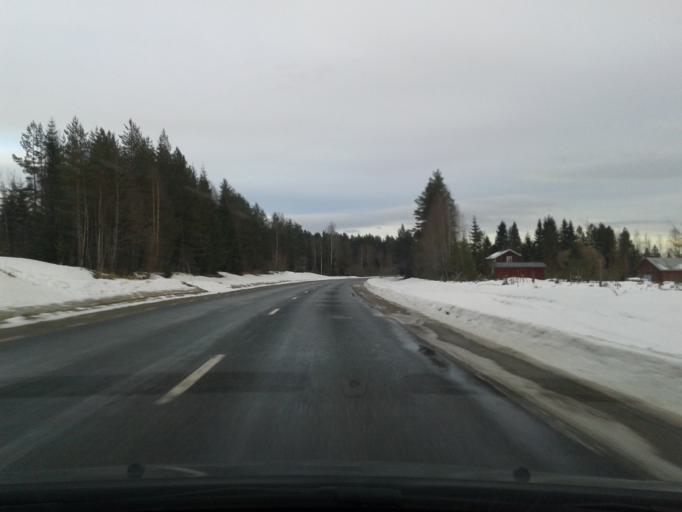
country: SE
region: Vaesternorrland
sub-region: Solleftea Kommun
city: As
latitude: 63.4348
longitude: 16.9394
